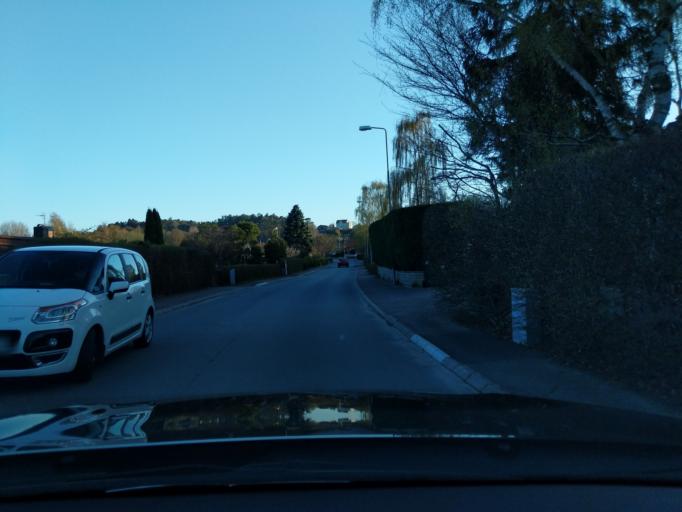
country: SE
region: Vaestra Goetaland
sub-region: Goteborg
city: Majorna
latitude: 57.6382
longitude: 11.9309
